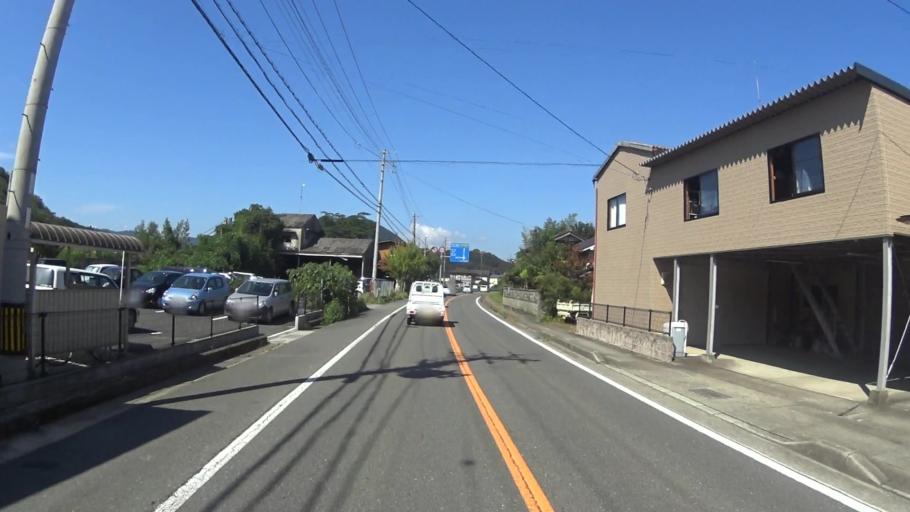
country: JP
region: Kyoto
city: Ayabe
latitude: 35.2914
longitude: 135.2723
